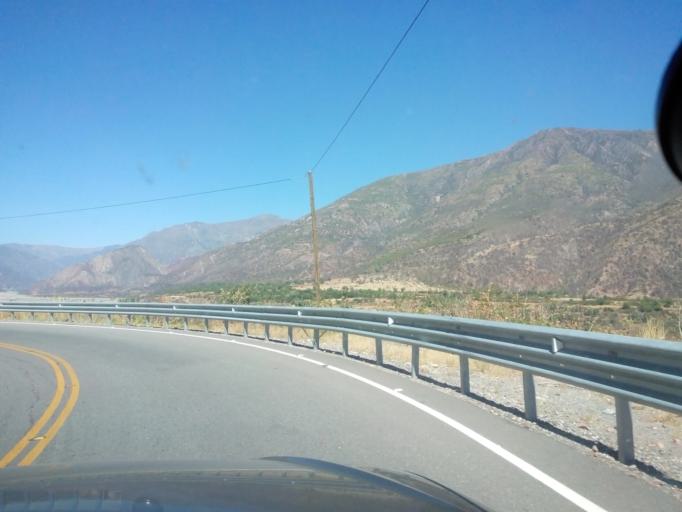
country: PE
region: Apurimac
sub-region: Chincheros
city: Chincheros
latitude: -13.4737
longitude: -73.8274
